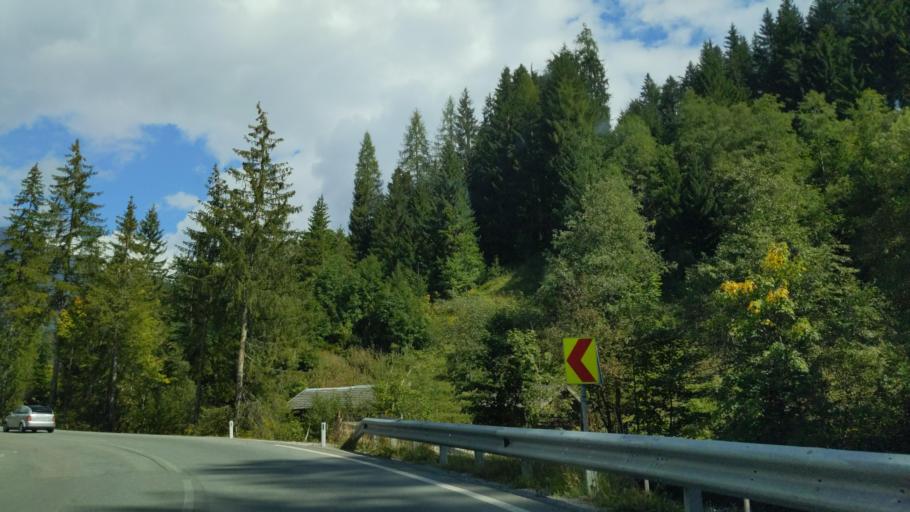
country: AT
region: Salzburg
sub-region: Politischer Bezirk Zell am See
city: Dienten am Hochkonig
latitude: 47.3946
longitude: 12.9601
